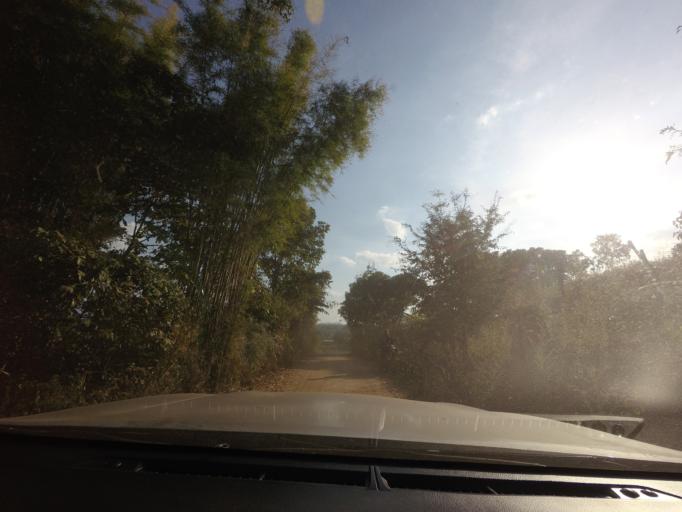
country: TH
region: Mae Hong Son
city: Wiang Nuea
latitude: 19.3996
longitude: 98.4064
